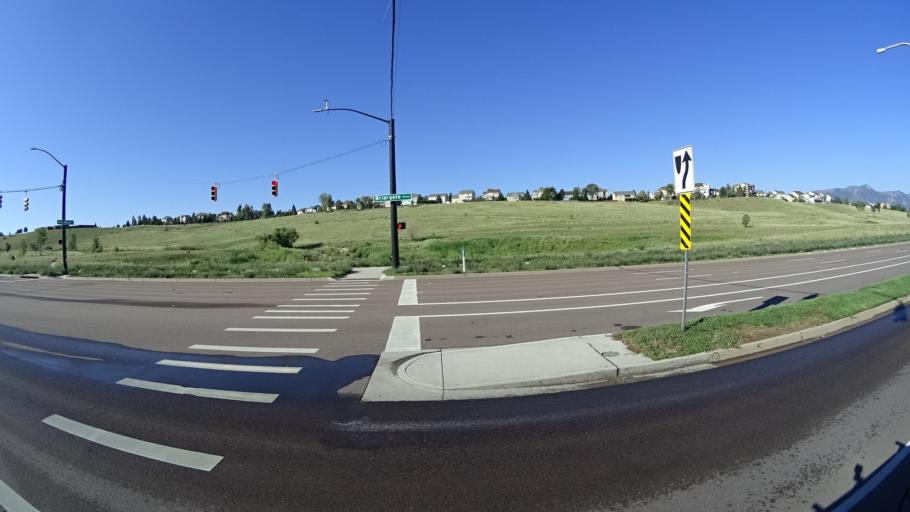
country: US
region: Colorado
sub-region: El Paso County
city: Black Forest
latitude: 38.9674
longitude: -104.7677
